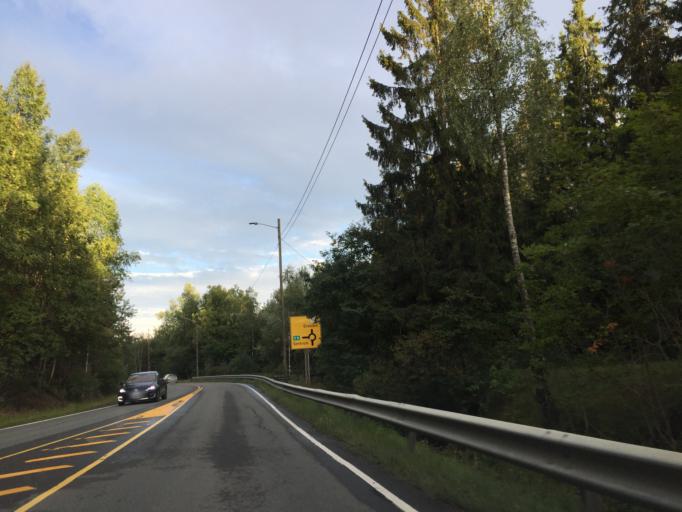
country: NO
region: Akershus
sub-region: Oppegard
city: Kolbotn
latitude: 59.8365
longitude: 10.8362
